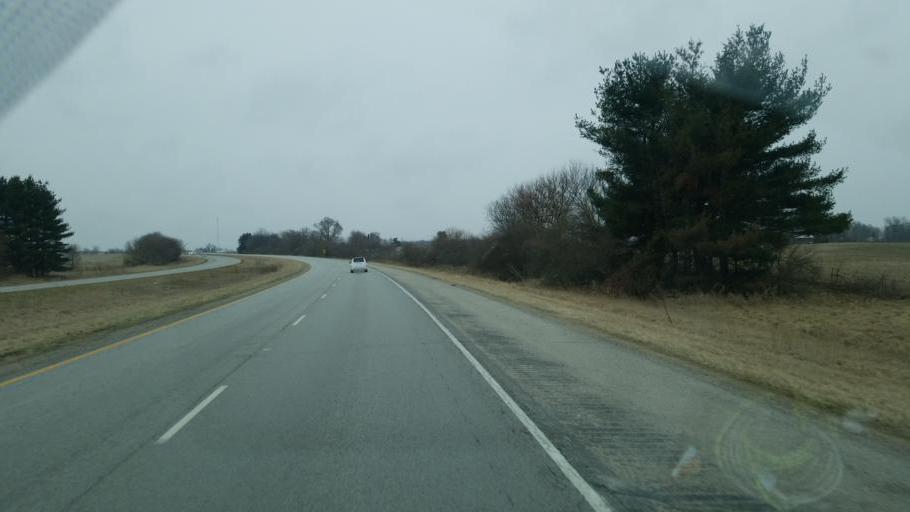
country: US
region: Indiana
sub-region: Miami County
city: Peru
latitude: 40.9008
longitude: -86.1589
